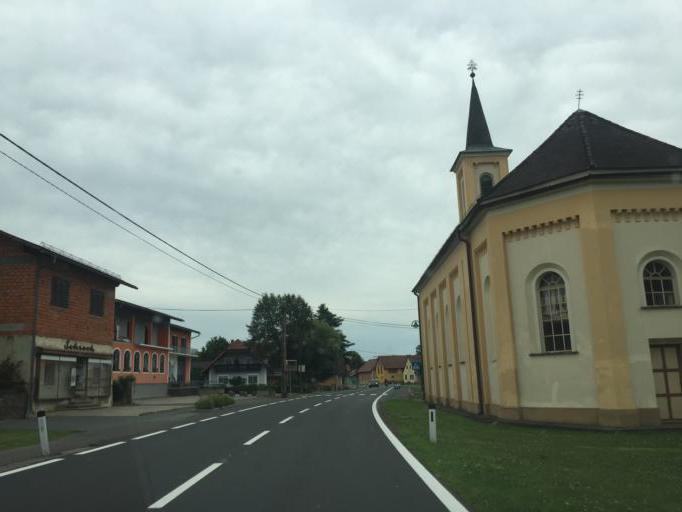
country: SI
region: Sentilj
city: Selnica ob Muri
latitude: 46.7115
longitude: 15.6958
